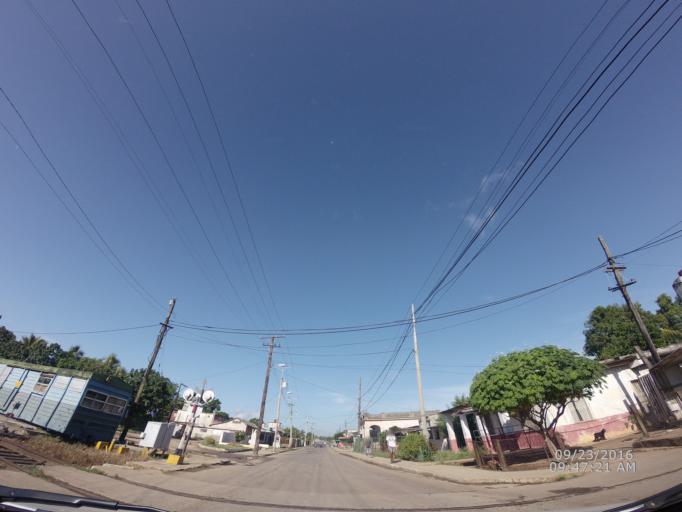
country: CU
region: La Habana
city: Santiago de las Vegas
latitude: 22.9520
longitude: -82.4150
